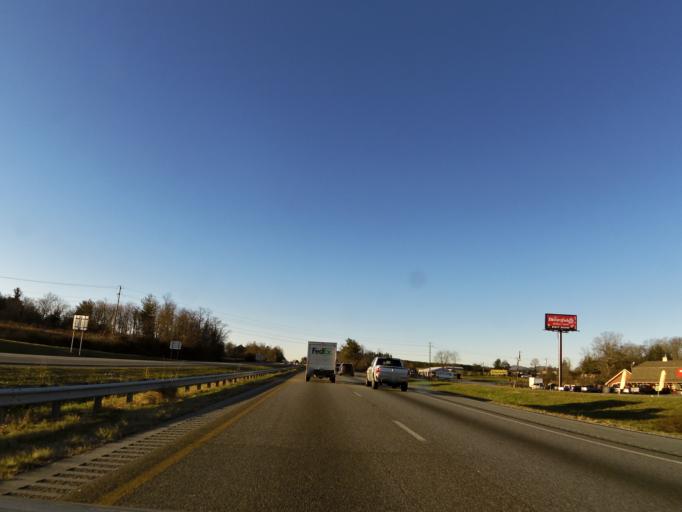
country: US
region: North Carolina
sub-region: Henderson County
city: East Flat Rock
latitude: 35.2983
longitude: -82.4078
